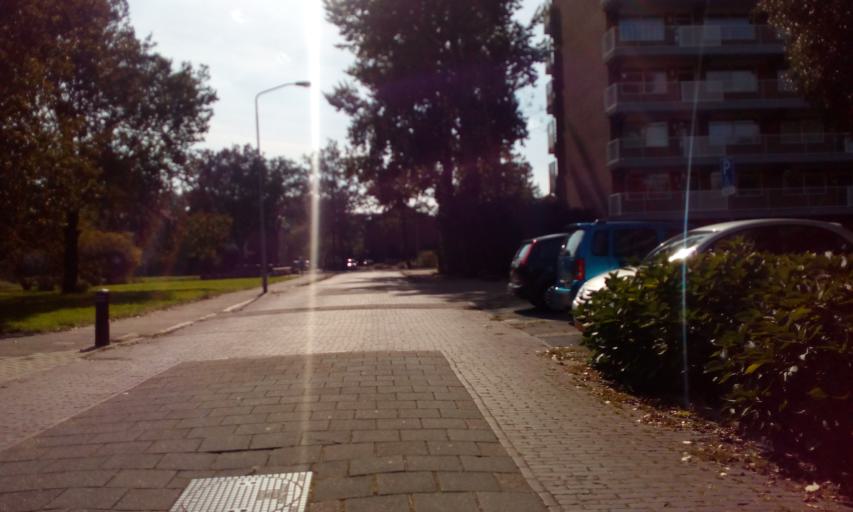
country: NL
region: South Holland
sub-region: Gemeente Voorschoten
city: Voorschoten
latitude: 52.1442
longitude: 4.4569
